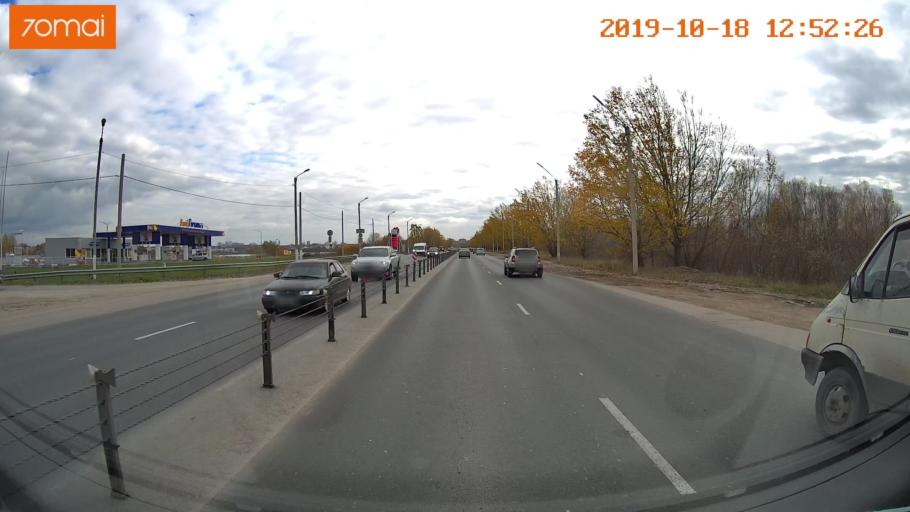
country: RU
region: Rjazan
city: Ryazan'
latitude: 54.6524
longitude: 39.6938
